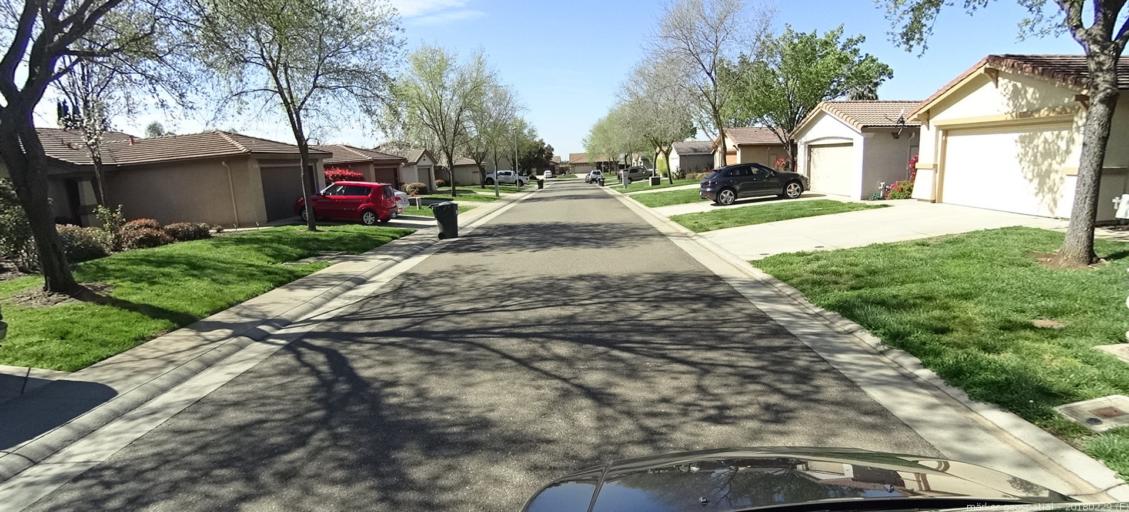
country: US
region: California
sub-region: Sacramento County
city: Rancho Cordova
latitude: 38.5447
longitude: -121.2855
